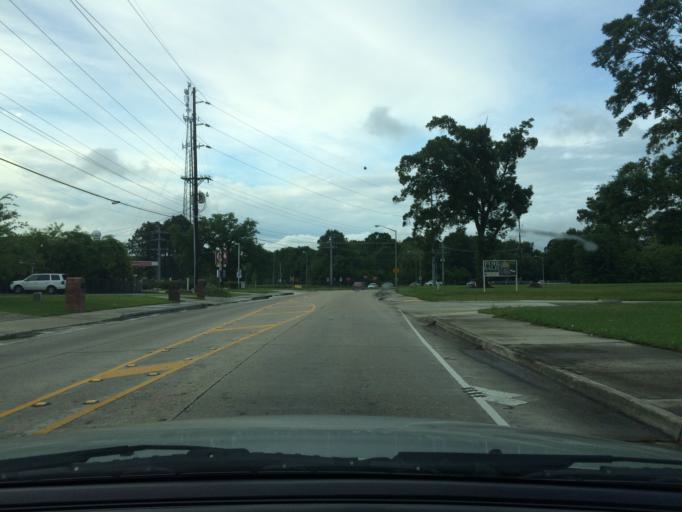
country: US
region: Louisiana
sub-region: Lafayette Parish
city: Scott
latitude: 30.2179
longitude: -92.0648
